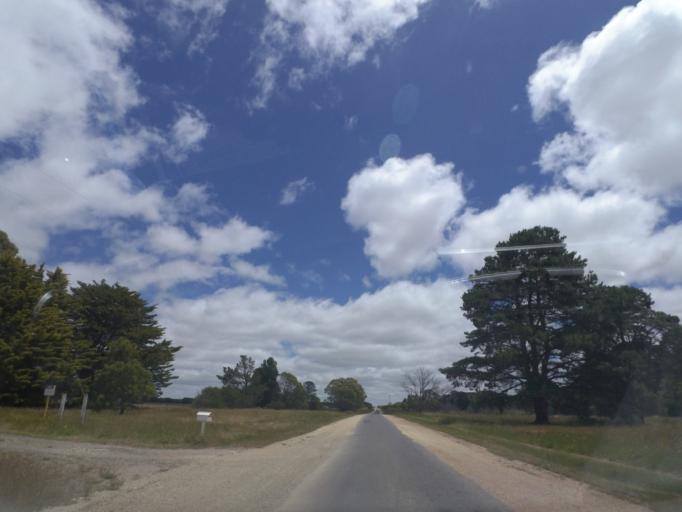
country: AU
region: Victoria
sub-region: Moorabool
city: Bacchus Marsh
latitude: -37.6398
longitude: 144.2821
